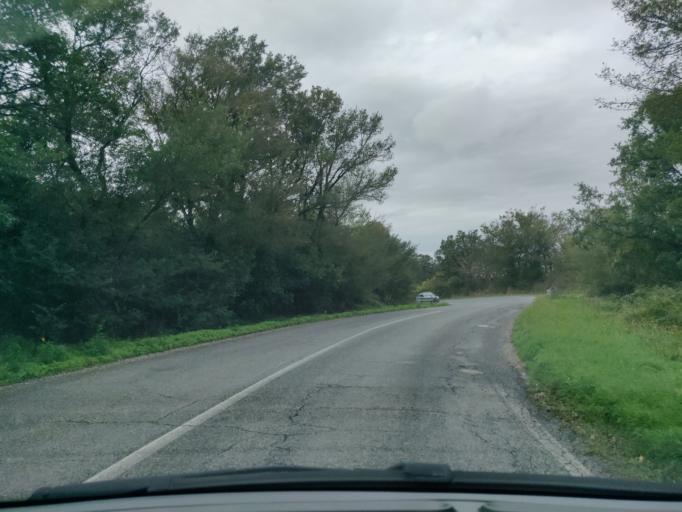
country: IT
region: Latium
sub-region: Citta metropolitana di Roma Capitale
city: Allumiere
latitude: 42.1439
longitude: 11.8863
